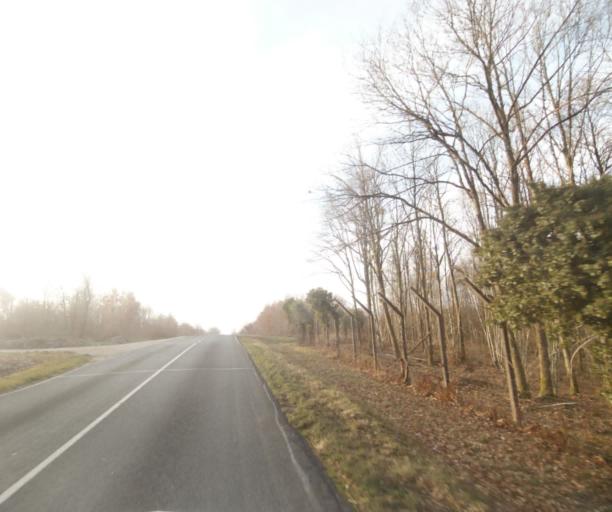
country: FR
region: Champagne-Ardenne
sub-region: Departement de la Haute-Marne
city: Chancenay
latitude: 48.6882
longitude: 4.9442
